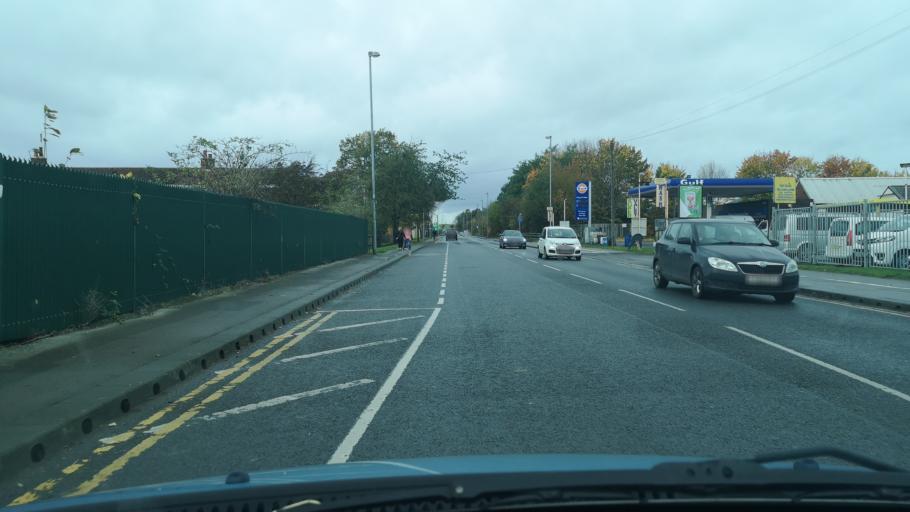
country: GB
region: England
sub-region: City and Borough of Wakefield
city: Featherstone
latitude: 53.6755
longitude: -1.3668
